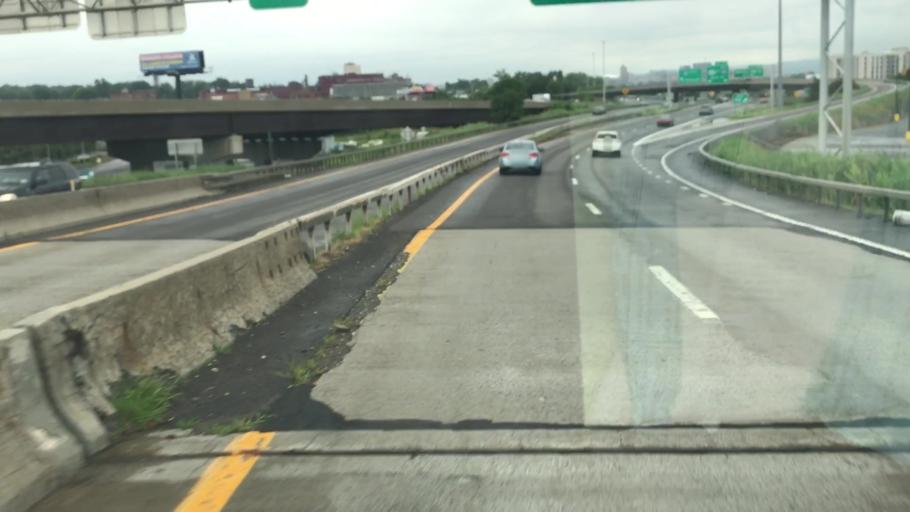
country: US
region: New York
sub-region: Onondaga County
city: Galeville
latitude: 43.0740
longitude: -76.1716
